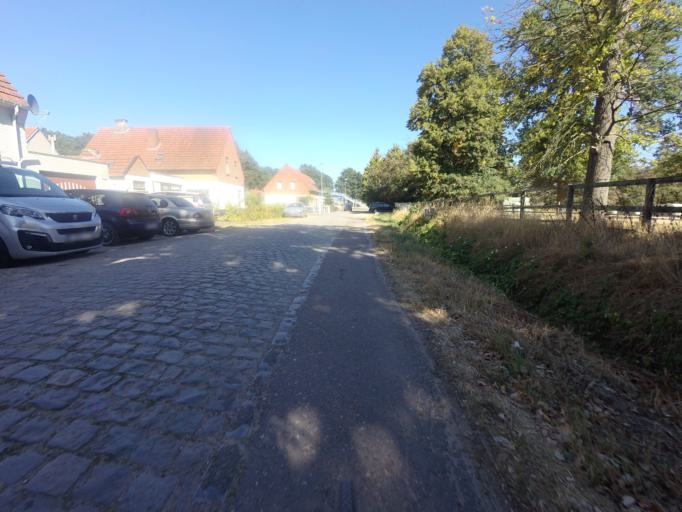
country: BE
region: Flanders
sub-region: Provincie Antwerpen
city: Turnhout
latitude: 51.3444
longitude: 4.9510
